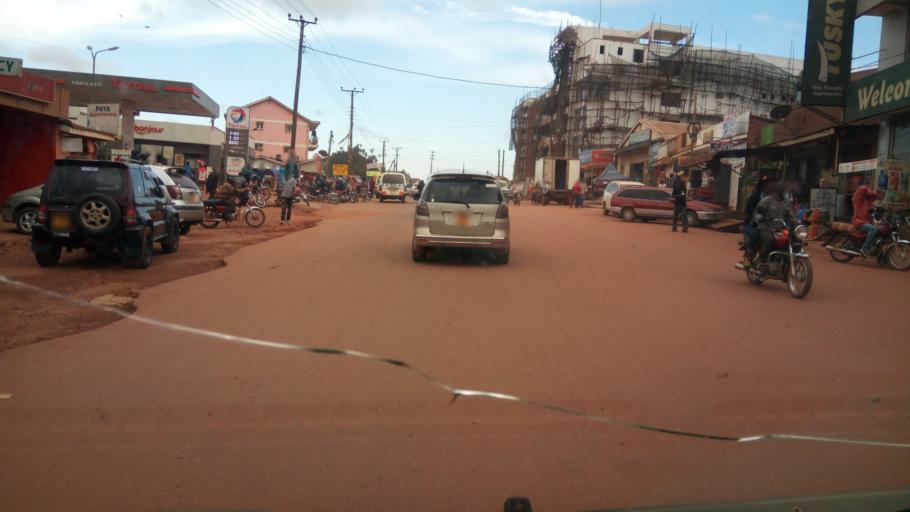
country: UG
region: Central Region
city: Kampala Central Division
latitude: 0.3251
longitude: 32.5593
